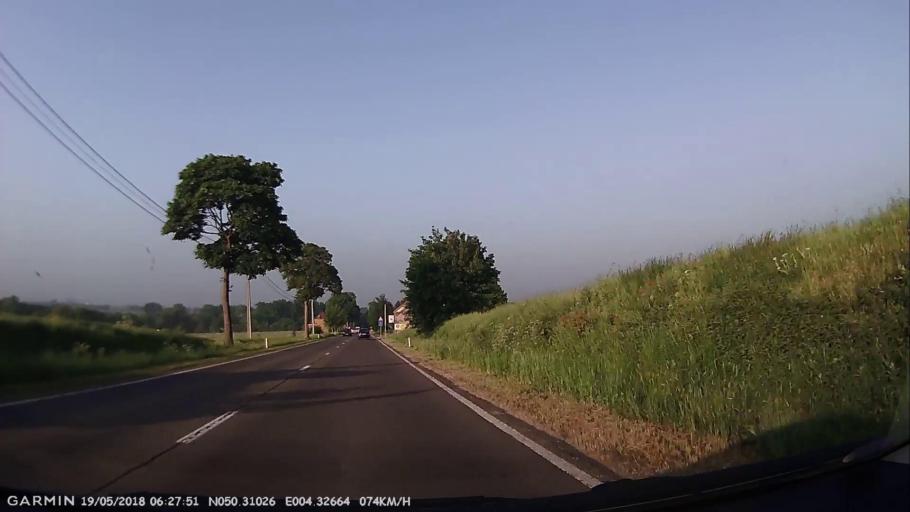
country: BE
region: Wallonia
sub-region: Province du Hainaut
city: Thuin
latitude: 50.3103
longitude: 4.3266
